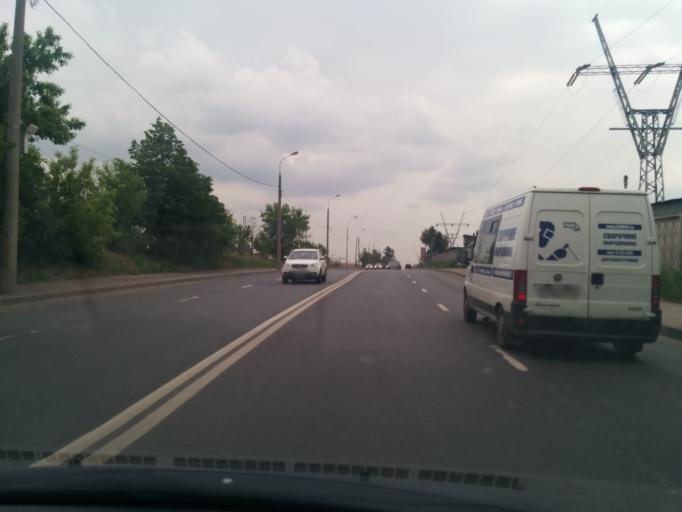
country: RU
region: Moscow
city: Likhobory
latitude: 55.8437
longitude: 37.5613
